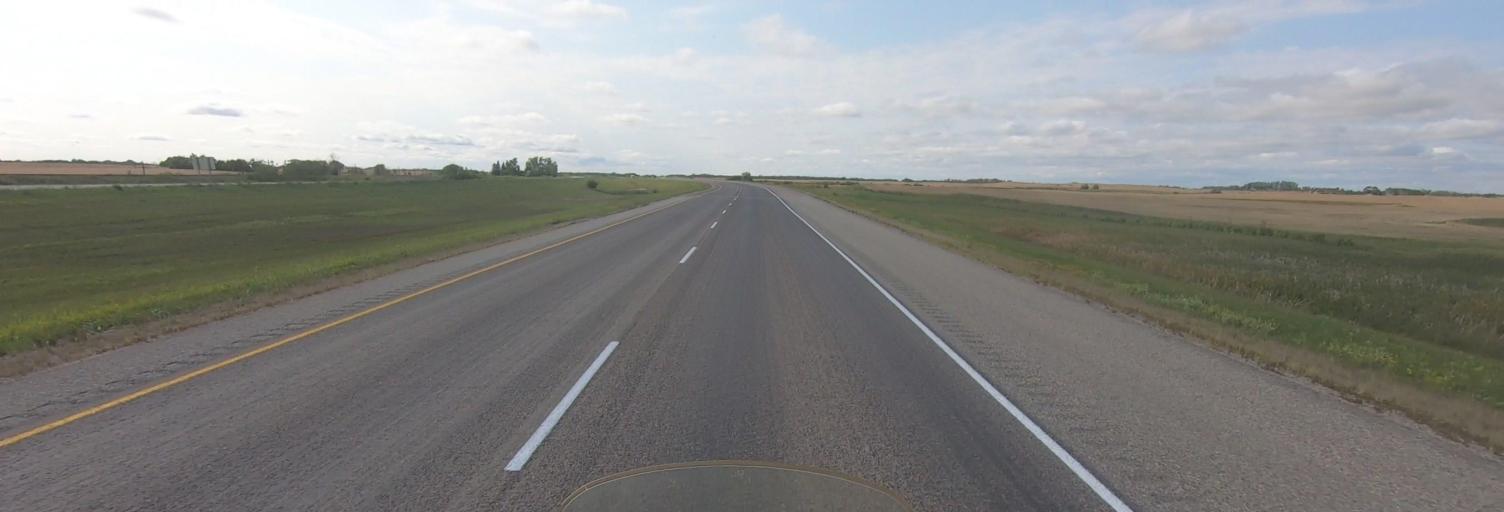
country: CA
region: Saskatchewan
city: Moosomin
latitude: 50.0507
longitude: -101.4257
